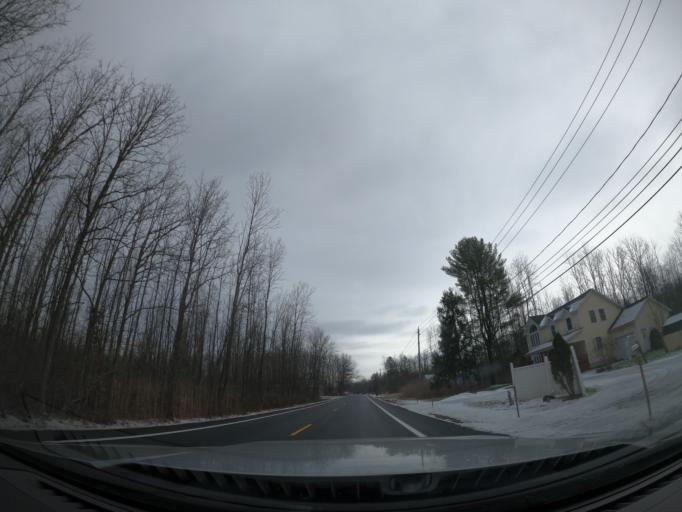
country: US
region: New York
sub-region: Madison County
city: Bridgeport
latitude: 43.1403
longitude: -75.9806
